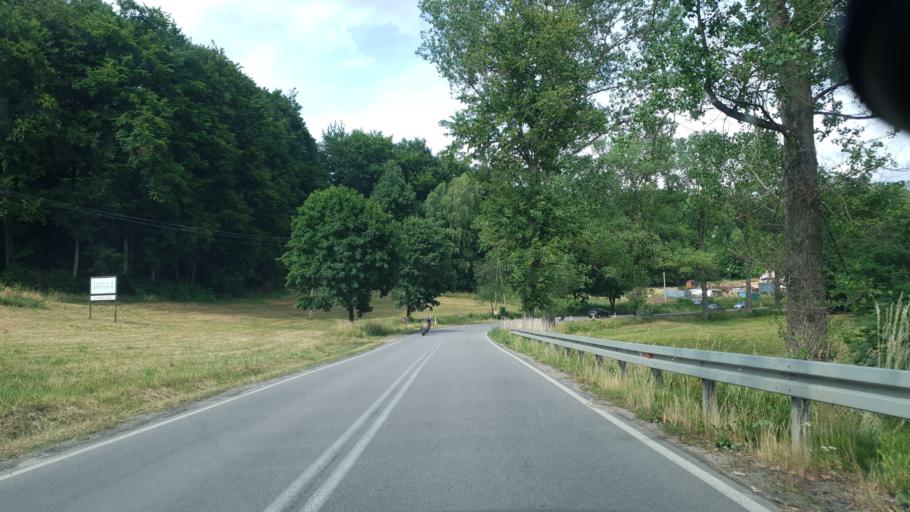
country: PL
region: Pomeranian Voivodeship
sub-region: Powiat kartuski
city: Chmielno
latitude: 54.2963
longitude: 18.1370
